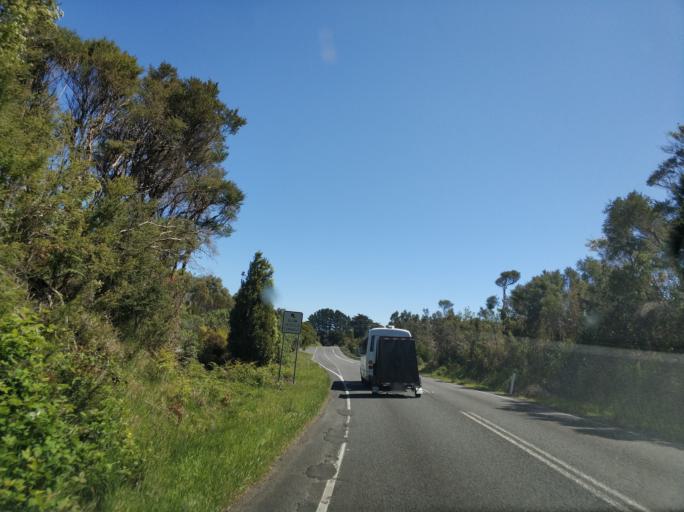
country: AU
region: Victoria
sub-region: Colac-Otway
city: Apollo Bay
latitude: -38.7364
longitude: 143.2953
